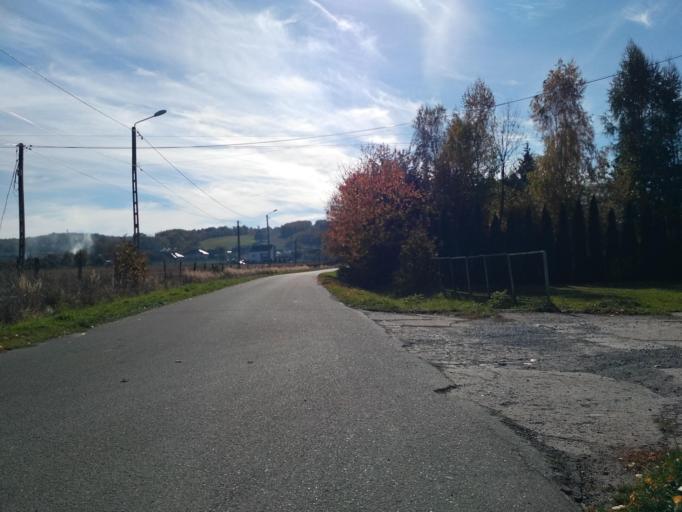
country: PL
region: Subcarpathian Voivodeship
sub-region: Powiat ropczycko-sedziszowski
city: Iwierzyce
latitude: 50.0595
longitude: 21.7862
